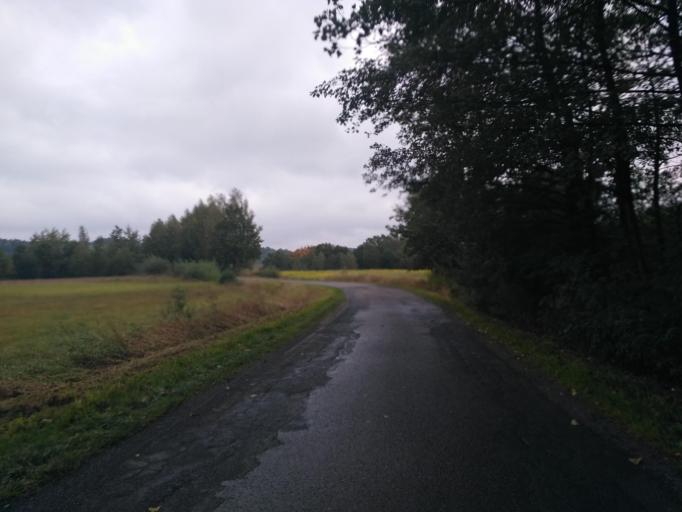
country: PL
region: Subcarpathian Voivodeship
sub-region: Powiat debicki
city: Brzostek
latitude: 49.9350
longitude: 21.4478
